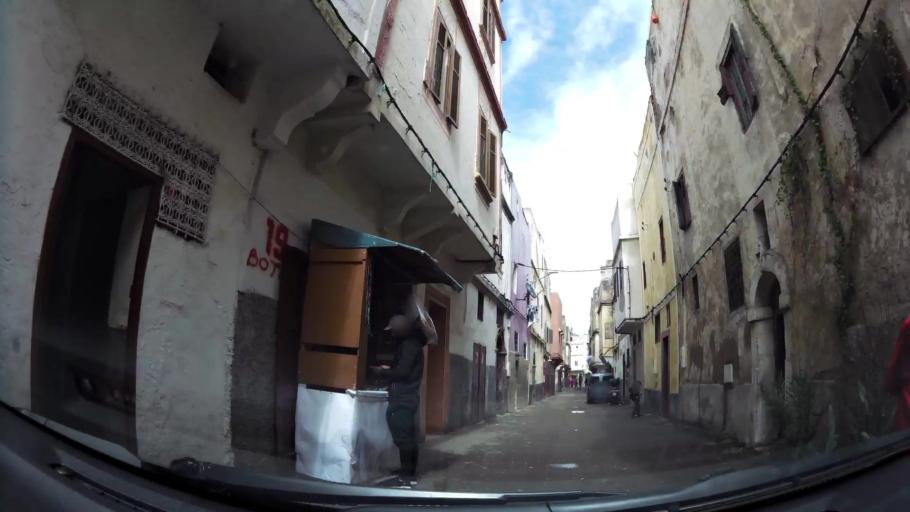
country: MA
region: Grand Casablanca
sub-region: Casablanca
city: Casablanca
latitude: 33.5752
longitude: -7.6084
